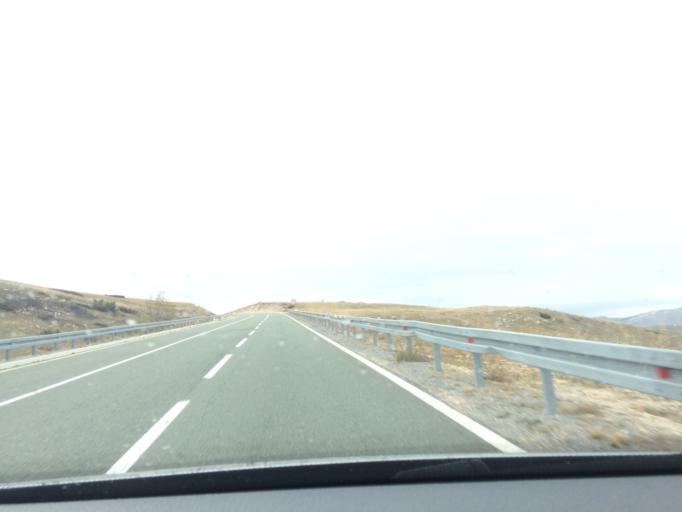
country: ME
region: Opstina Zabljak
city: Zabljak
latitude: 43.0772
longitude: 19.1023
